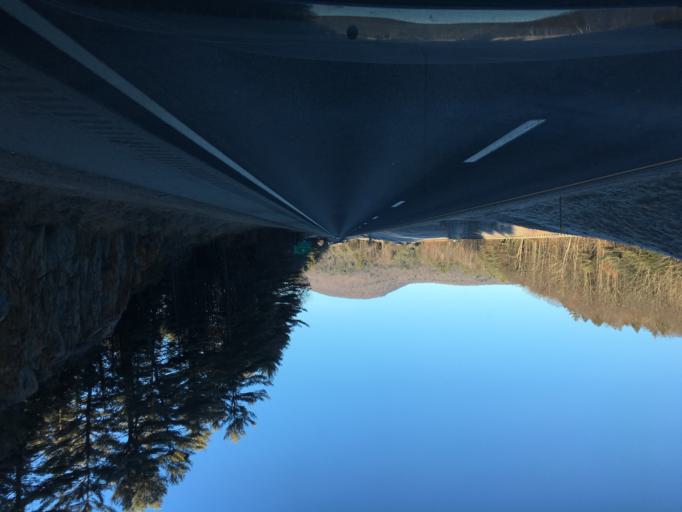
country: US
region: New Hampshire
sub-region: Grafton County
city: Plymouth
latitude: 43.7923
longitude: -71.6745
